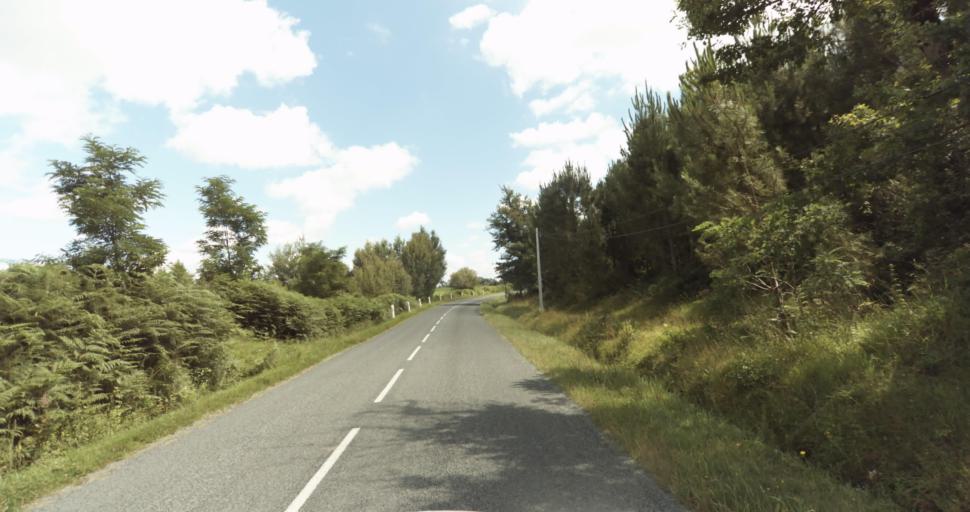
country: FR
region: Aquitaine
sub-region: Departement de la Gironde
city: Bazas
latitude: 44.4592
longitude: -0.1903
